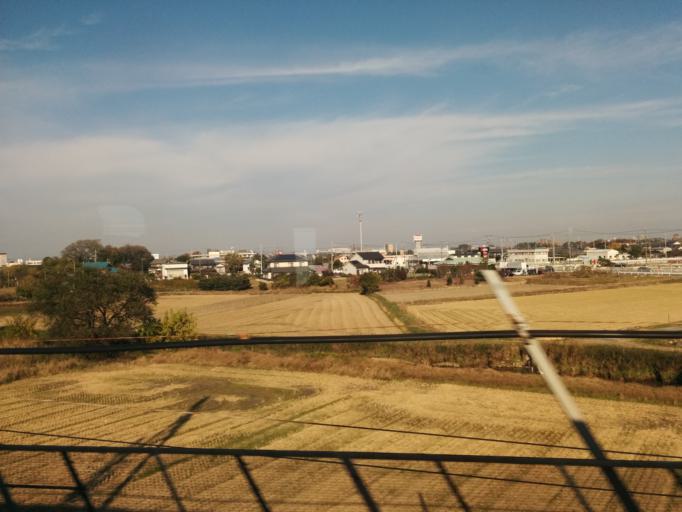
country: JP
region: Aichi
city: Inazawa
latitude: 35.2409
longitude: 136.7780
